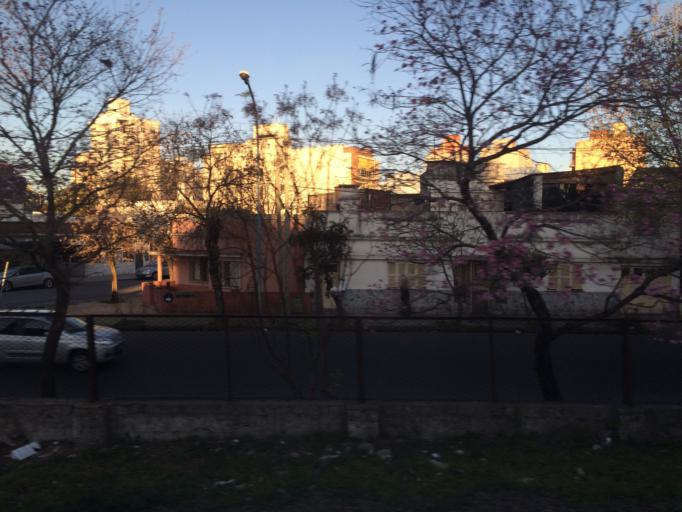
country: AR
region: Buenos Aires
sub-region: Partido de Lanus
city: Lanus
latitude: -34.7114
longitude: -58.3917
